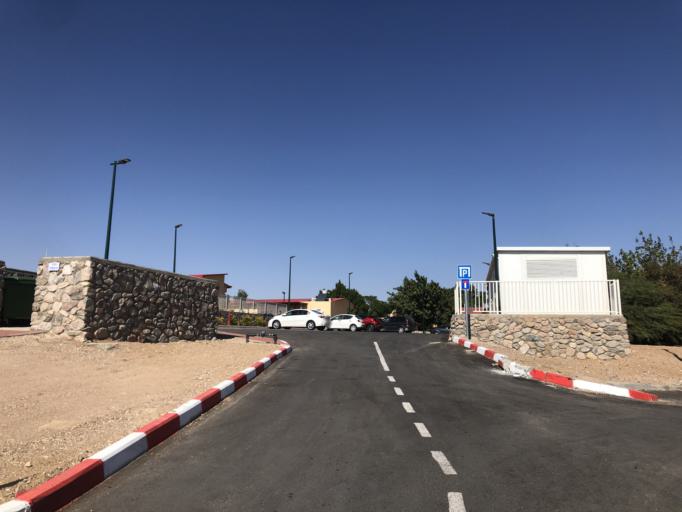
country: IL
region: Southern District
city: Eilat
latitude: 29.5813
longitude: 34.9605
